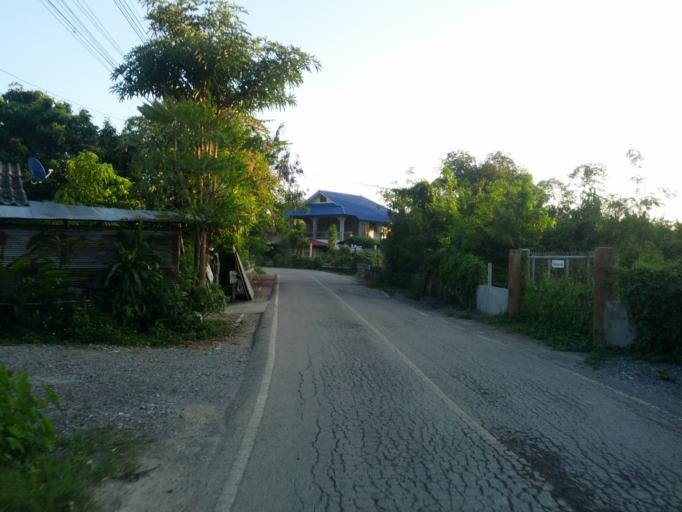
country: TH
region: Chiang Mai
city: San Kamphaeng
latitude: 18.7697
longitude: 99.0962
